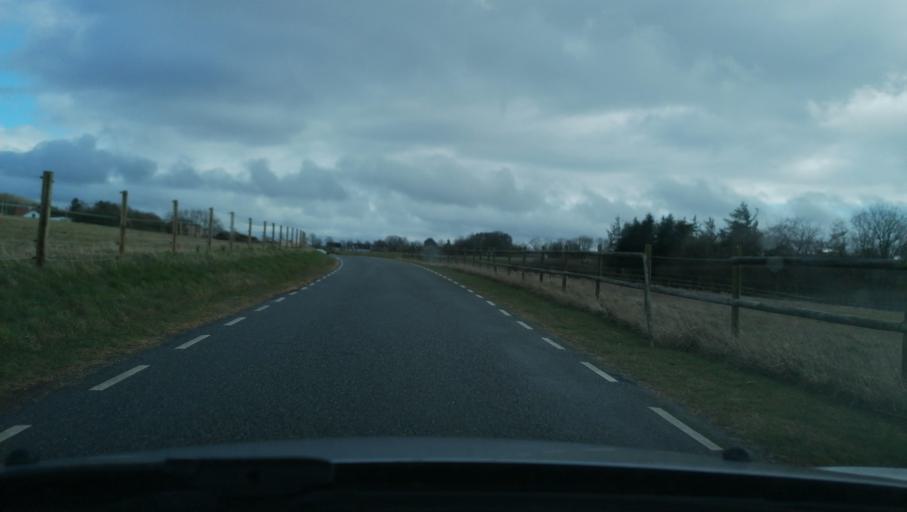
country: DK
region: Zealand
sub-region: Odsherred Kommune
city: Horve
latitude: 55.7456
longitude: 11.3986
